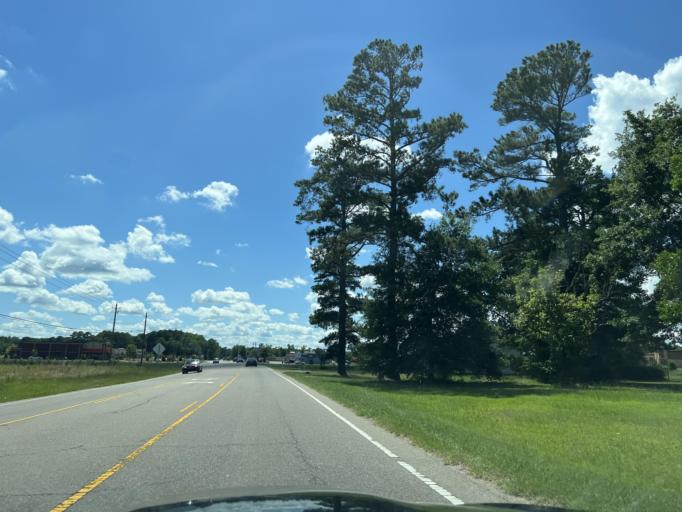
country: US
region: North Carolina
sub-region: Lee County
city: Sanford
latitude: 35.4380
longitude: -79.2144
